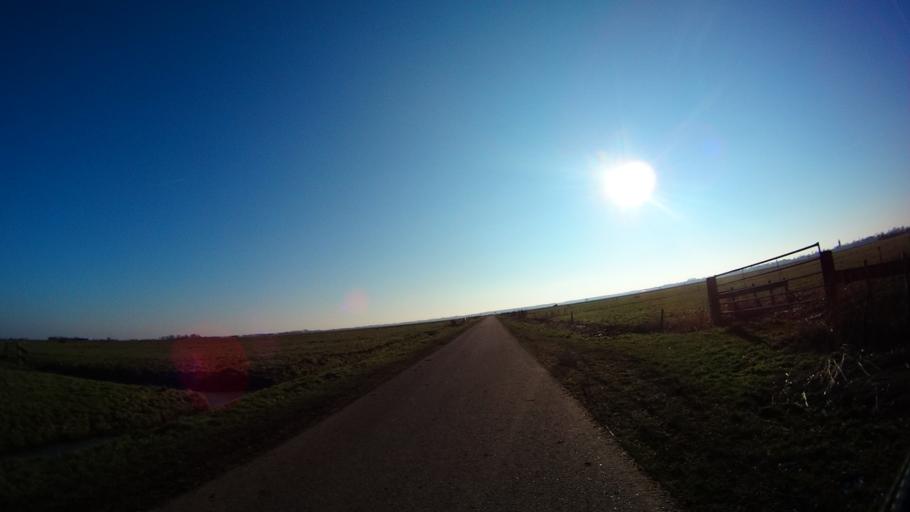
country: NL
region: Utrecht
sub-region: Gemeente Baarn
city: Baarn
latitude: 52.2590
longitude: 5.2890
